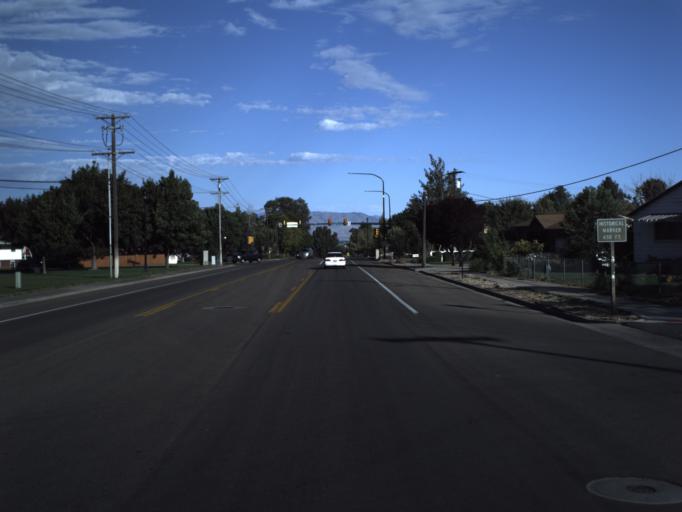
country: US
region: Utah
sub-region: Utah County
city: Spanish Fork
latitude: 40.1034
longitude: -111.6390
